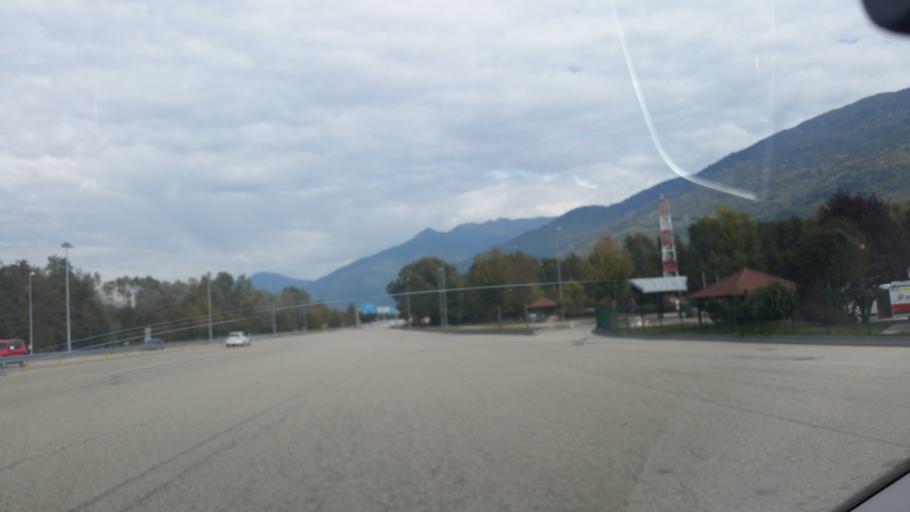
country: FR
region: Rhone-Alpes
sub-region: Departement de la Savoie
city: Sainte-Helene-sur-Isere
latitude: 45.6202
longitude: 6.3128
